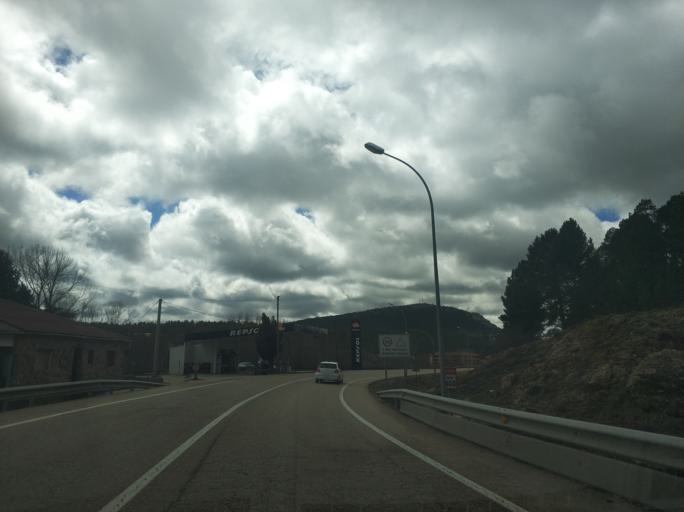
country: ES
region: Castille and Leon
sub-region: Provincia de Soria
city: San Leonardo de Yague
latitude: 41.8320
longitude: -3.0558
